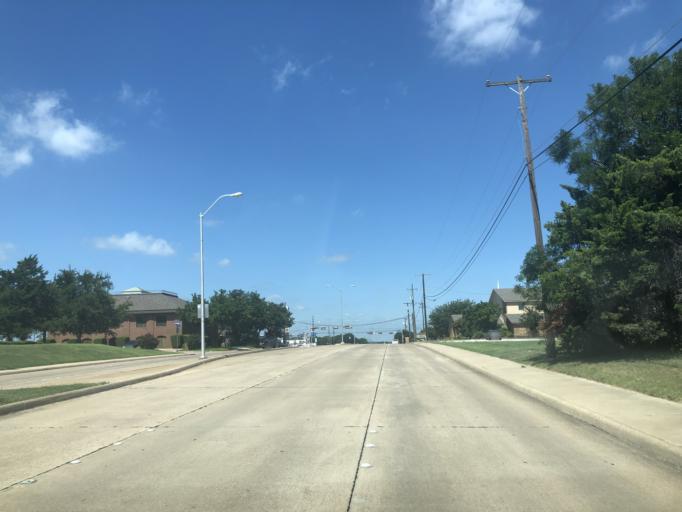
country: US
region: Texas
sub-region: Dallas County
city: Duncanville
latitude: 32.6473
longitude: -96.9407
